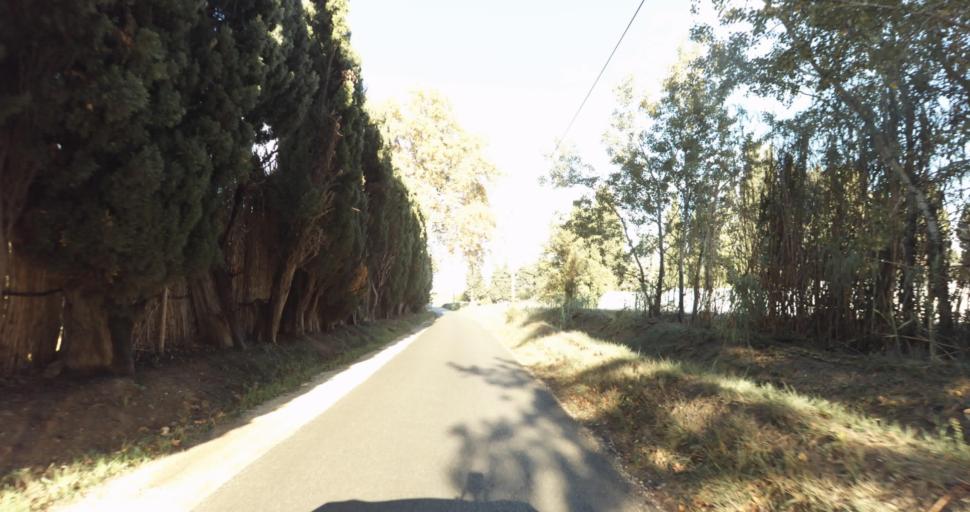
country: FR
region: Provence-Alpes-Cote d'Azur
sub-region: Departement des Bouches-du-Rhone
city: Rognonas
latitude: 43.8921
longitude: 4.8069
